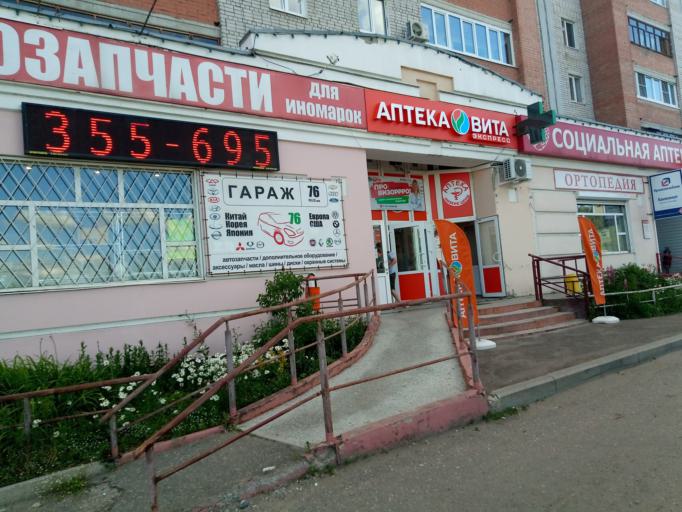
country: RU
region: Jaroslavl
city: Yaroslavl
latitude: 57.6396
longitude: 39.9616
